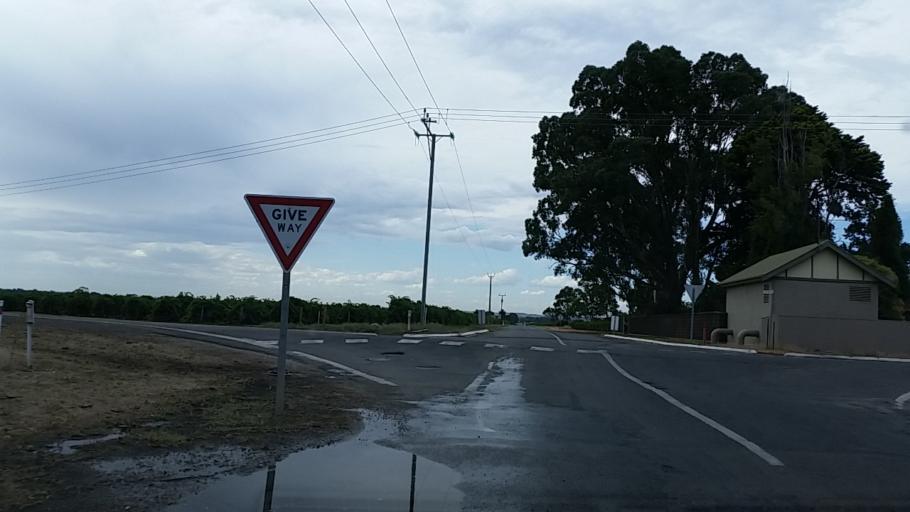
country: AU
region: South Australia
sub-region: Barossa
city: Nuriootpa
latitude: -34.4906
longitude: 139.0150
